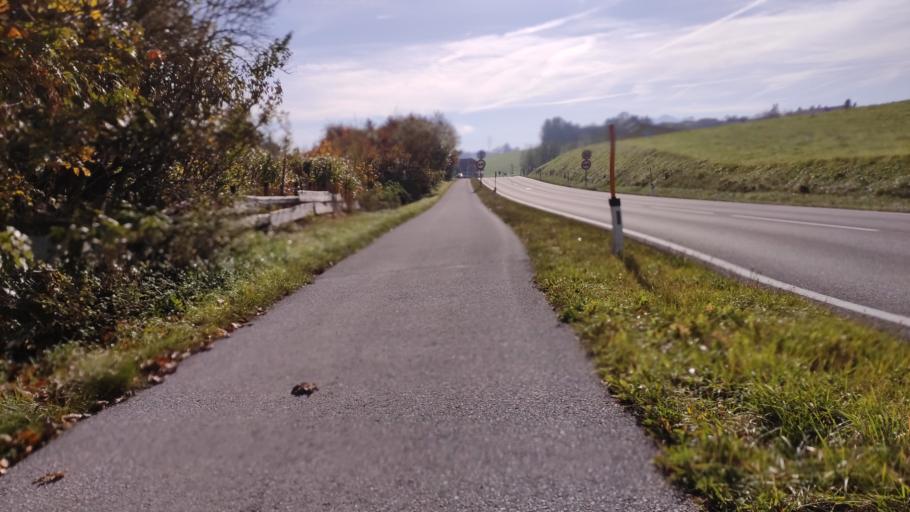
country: AT
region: Salzburg
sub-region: Politischer Bezirk Salzburg-Umgebung
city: Koppl
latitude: 47.8233
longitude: 13.1498
